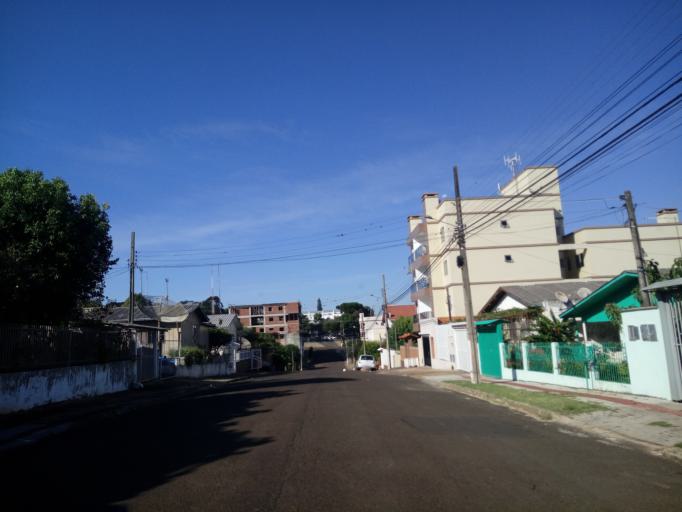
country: BR
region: Santa Catarina
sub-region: Chapeco
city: Chapeco
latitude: -27.0958
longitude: -52.6446
